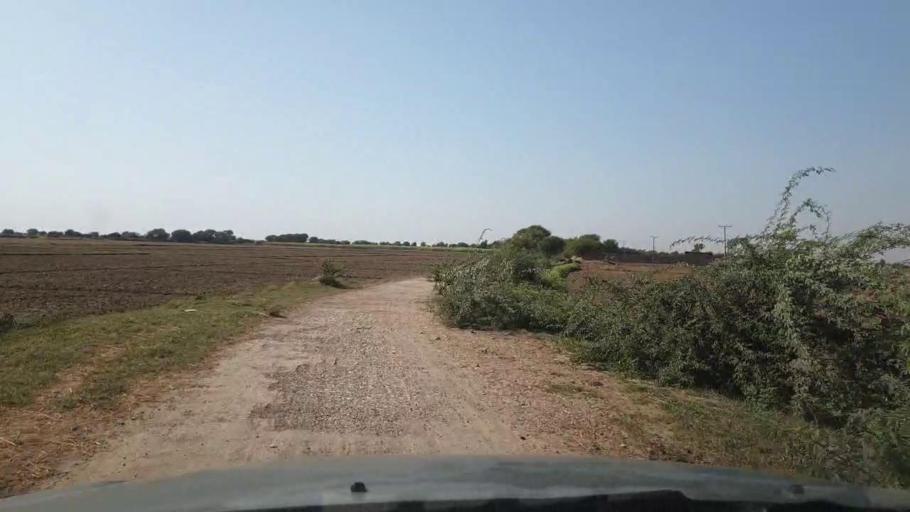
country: PK
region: Sindh
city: Bulri
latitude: 24.9512
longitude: 68.3233
